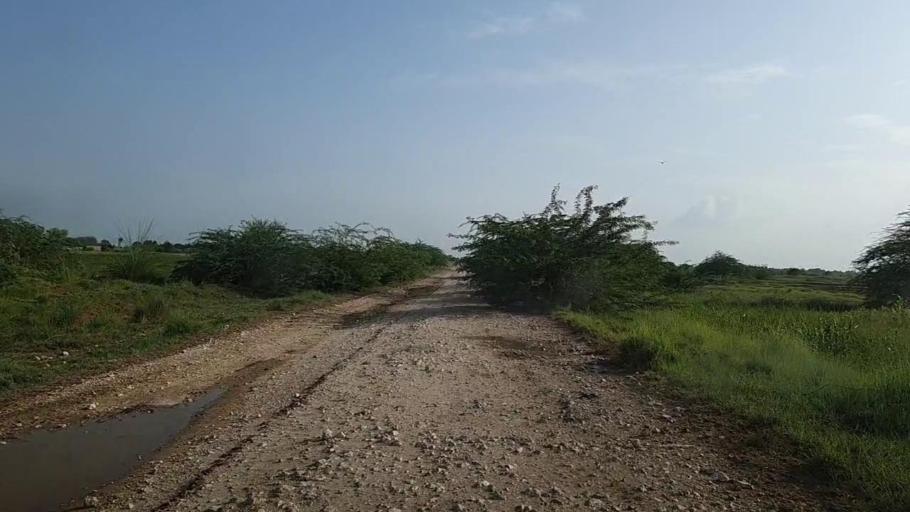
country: PK
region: Sindh
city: Pad Idan
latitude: 26.8136
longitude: 68.2364
